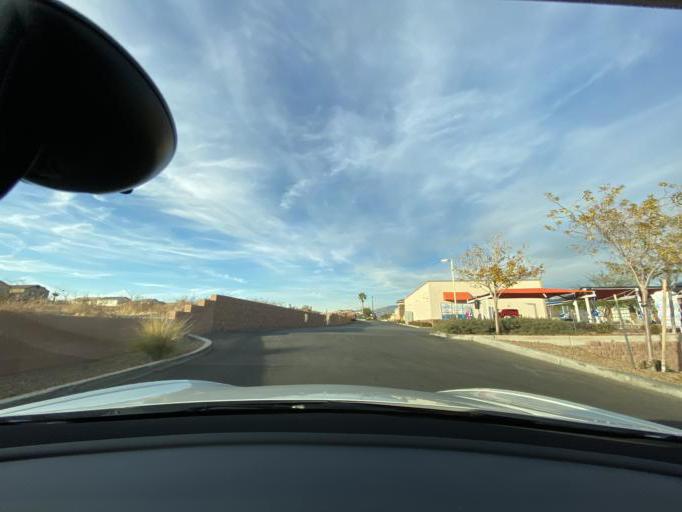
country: US
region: Nevada
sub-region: Clark County
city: Summerlin South
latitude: 36.2837
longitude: -115.2889
